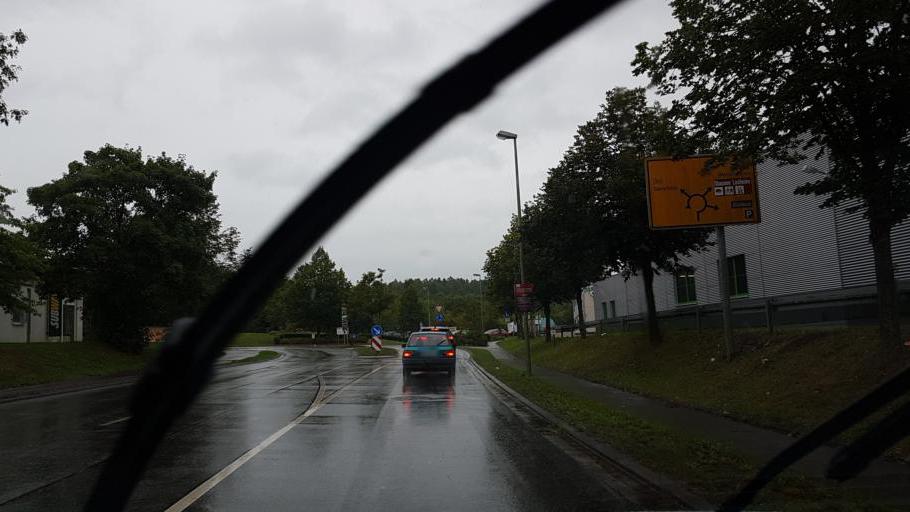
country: DE
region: Saarland
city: Losheim
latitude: 49.5122
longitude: 6.7546
